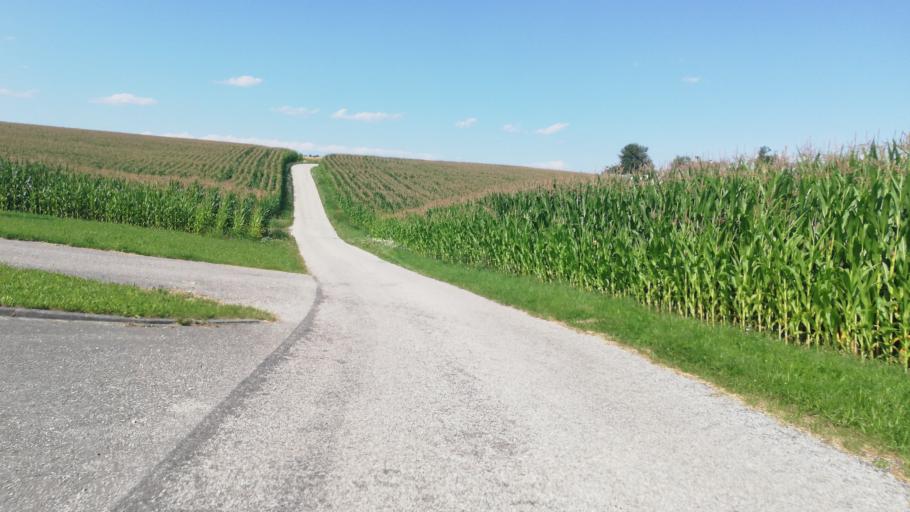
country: AT
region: Upper Austria
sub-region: Wels-Land
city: Edt bei Lambach
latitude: 48.1587
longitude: 13.8990
